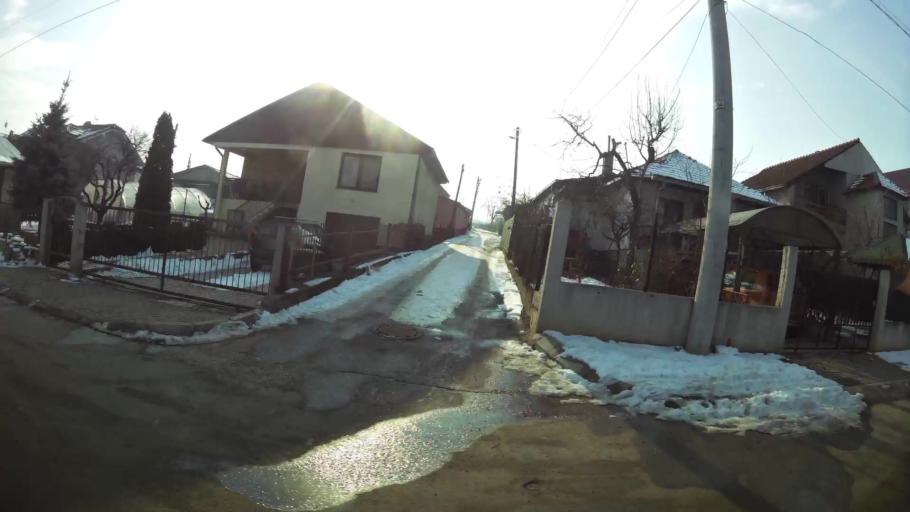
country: MK
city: Creshevo
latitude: 42.0130
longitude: 21.4952
